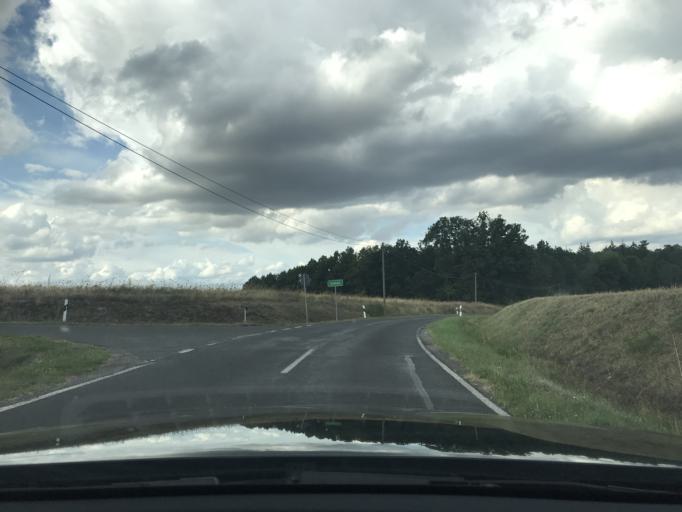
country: DE
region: Bavaria
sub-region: Regierungsbezirk Unterfranken
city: Kirchlauter
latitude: 50.0809
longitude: 10.6944
